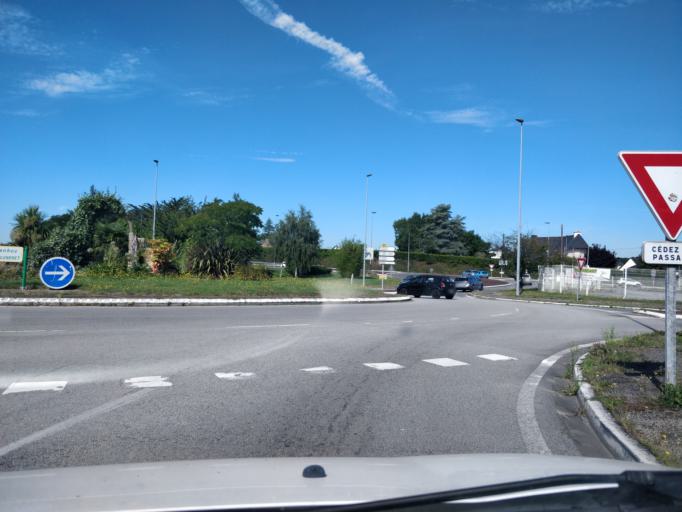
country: FR
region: Brittany
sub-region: Departement du Morbihan
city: Pluneret
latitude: 47.6672
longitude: -2.9642
